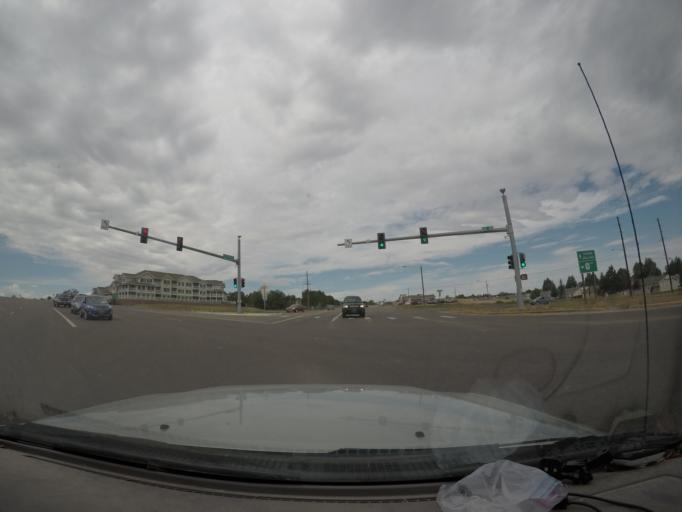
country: US
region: Wyoming
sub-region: Laramie County
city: Fox Farm-College
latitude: 41.1455
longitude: -104.7559
